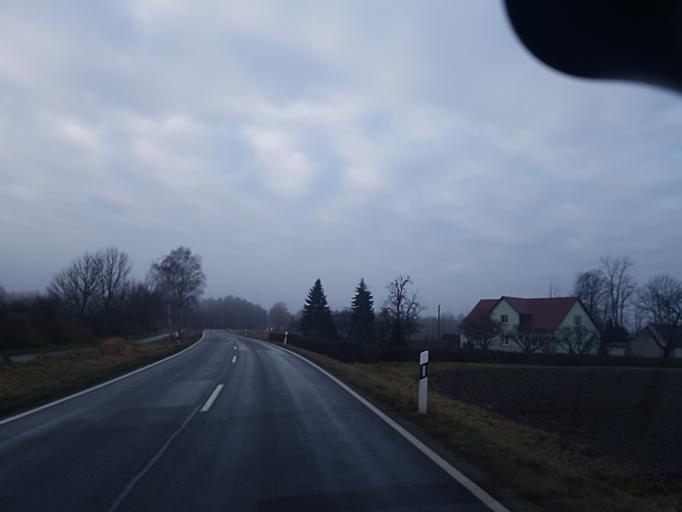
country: DE
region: Brandenburg
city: Finsterwalde
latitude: 51.6032
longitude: 13.7138
